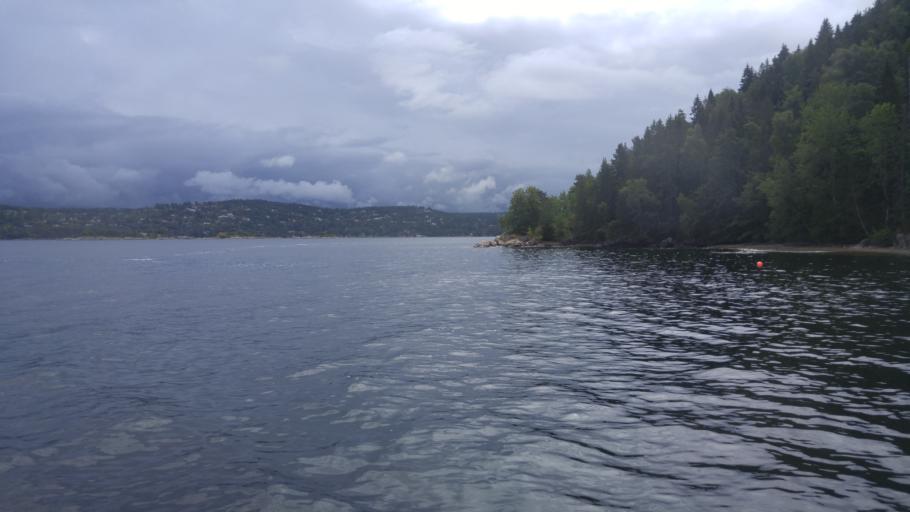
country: NO
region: Akershus
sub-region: Nesodden
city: Fagerstrand
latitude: 59.7023
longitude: 10.5685
